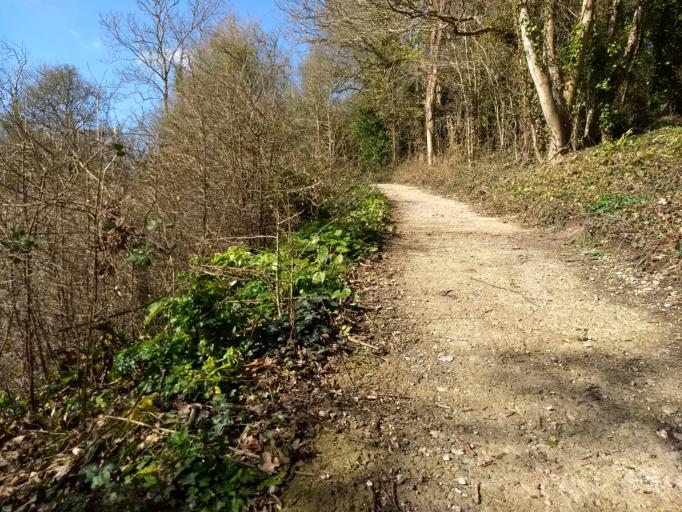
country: GB
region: England
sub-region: Isle of Wight
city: Seaview
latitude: 50.6998
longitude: -1.1042
